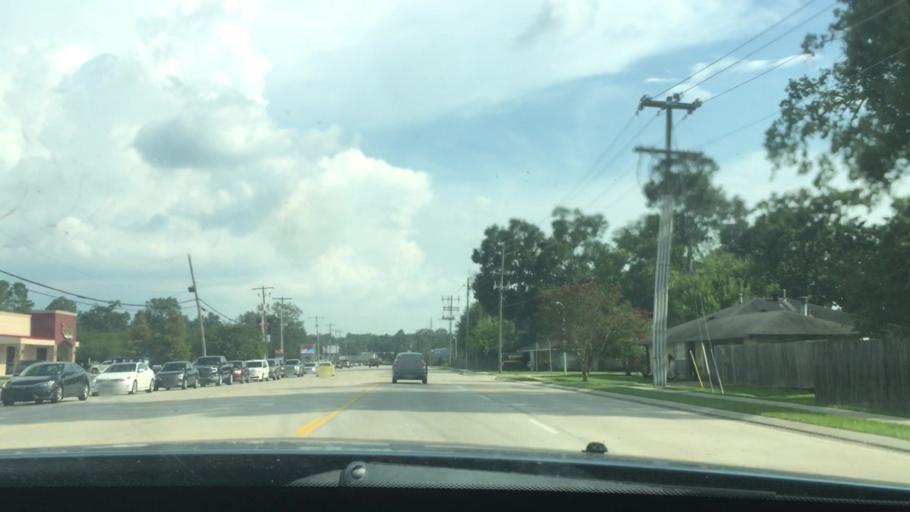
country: US
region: Louisiana
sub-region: East Baton Rouge Parish
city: Shenandoah
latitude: 30.4342
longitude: -91.0245
